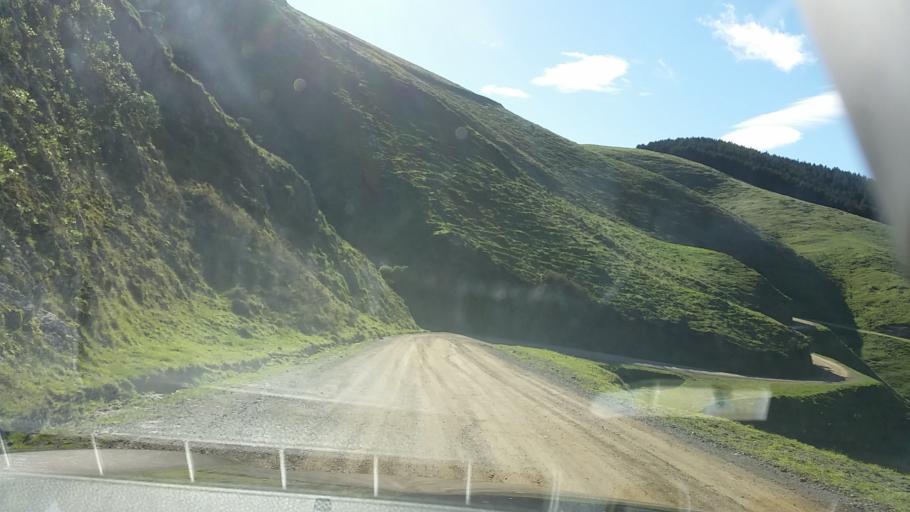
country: NZ
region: Marlborough
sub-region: Marlborough District
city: Picton
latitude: -40.9878
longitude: 173.8084
